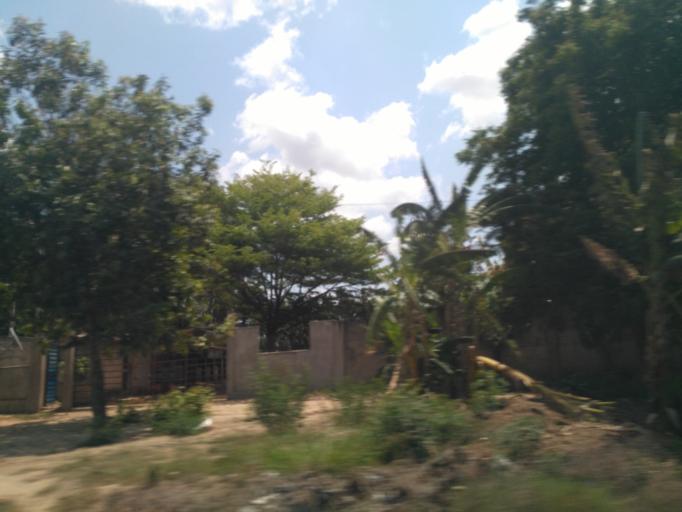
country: TZ
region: Dar es Salaam
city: Dar es Salaam
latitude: -6.8402
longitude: 39.3503
